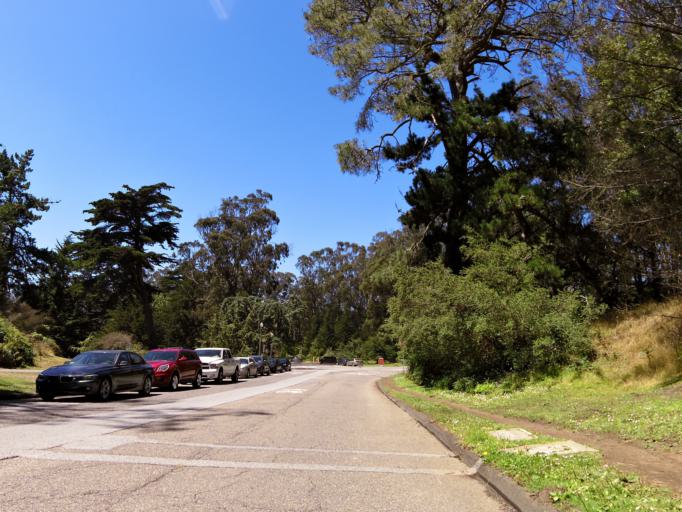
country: US
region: California
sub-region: San Francisco County
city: San Francisco
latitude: 37.7673
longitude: -122.4794
